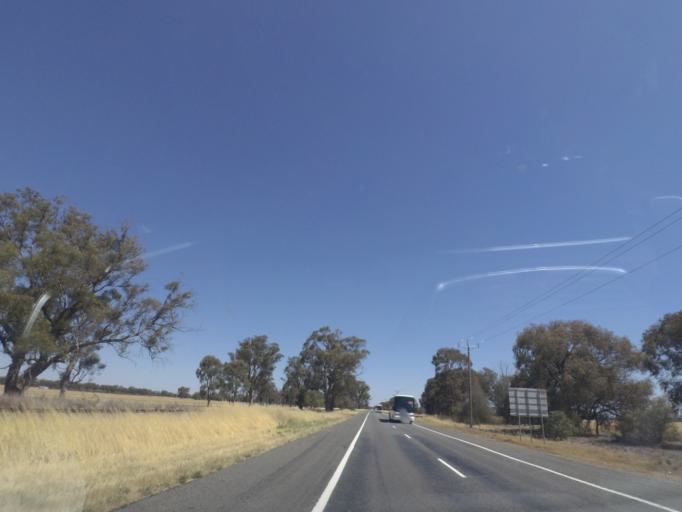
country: AU
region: Victoria
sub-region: Greater Shepparton
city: Shepparton
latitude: -36.2067
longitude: 145.4319
